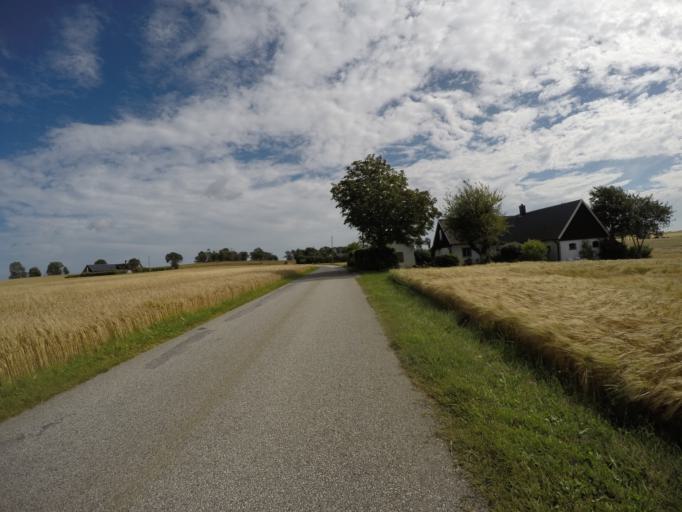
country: SE
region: Skane
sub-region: Simrishamns Kommun
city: Simrishamn
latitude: 55.4904
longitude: 14.2611
